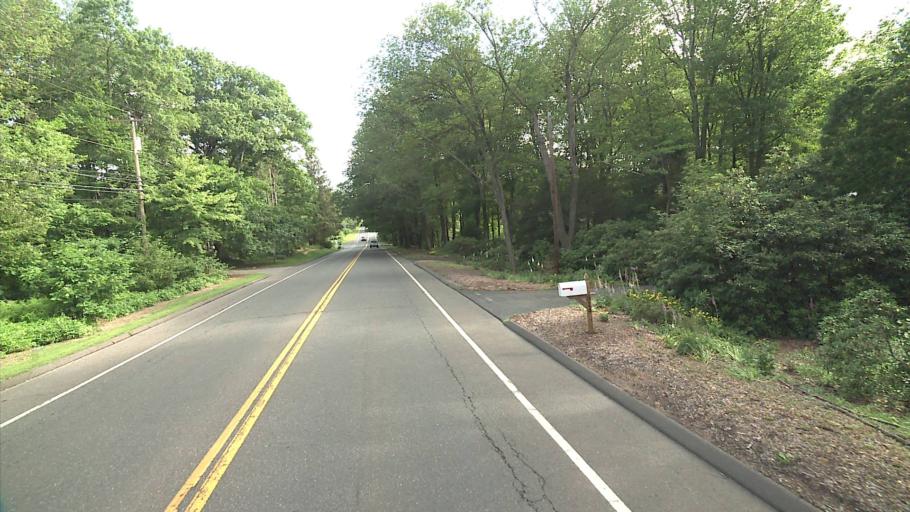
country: US
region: Connecticut
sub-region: New Haven County
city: Prospect
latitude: 41.4452
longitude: -72.9893
